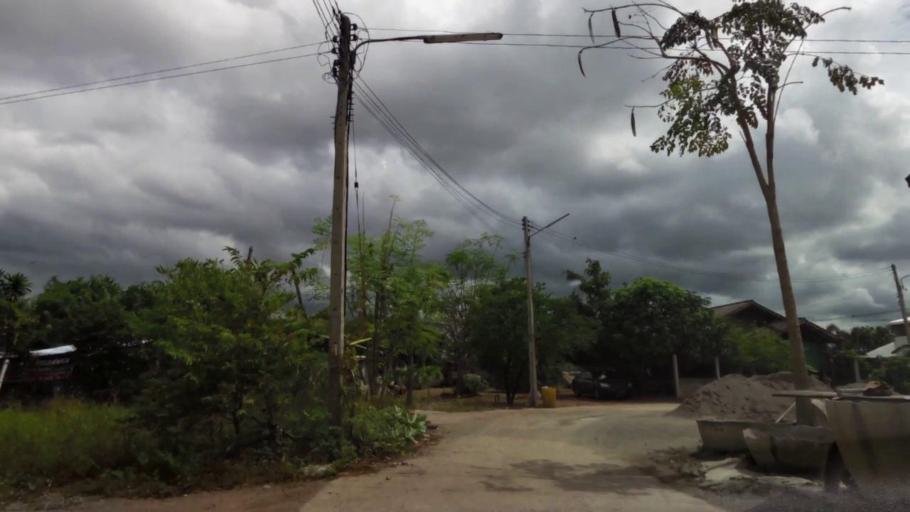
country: TH
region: Nakhon Sawan
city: Phai Sali
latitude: 15.5946
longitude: 100.6457
